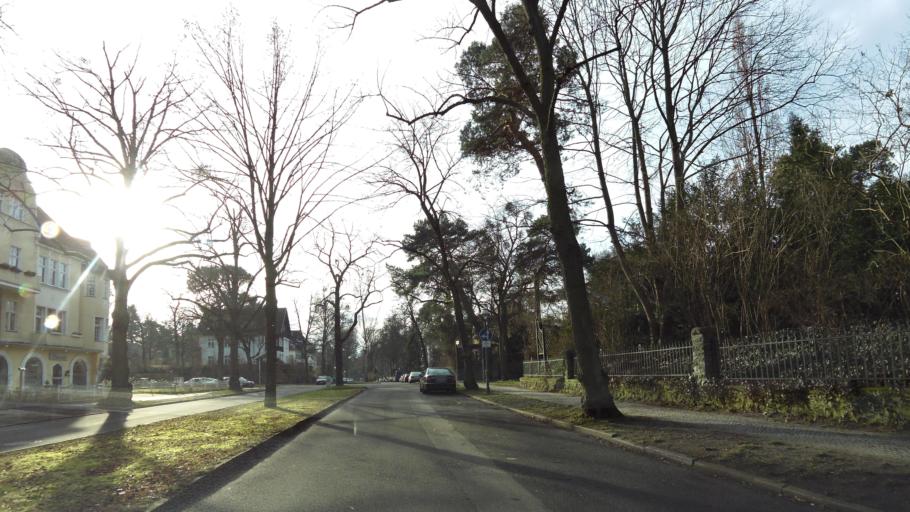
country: DE
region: Berlin
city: Nikolassee
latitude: 52.4282
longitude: 13.1964
